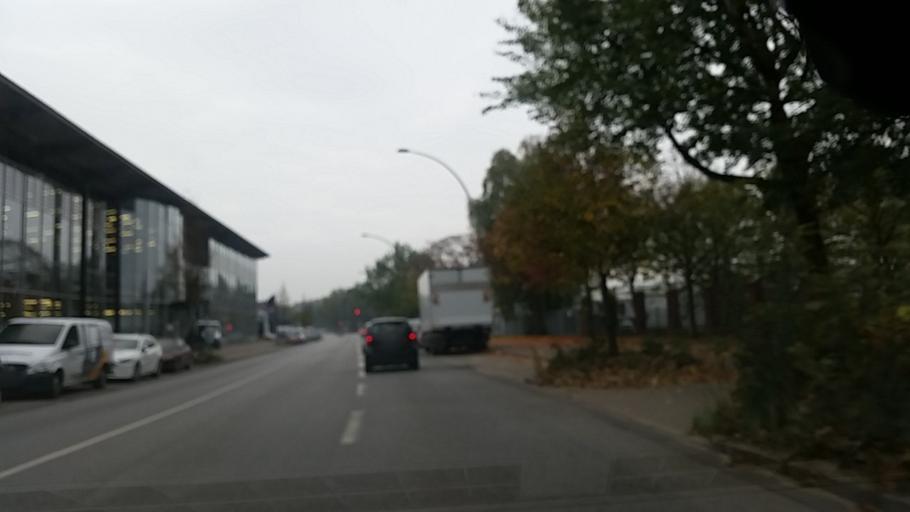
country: DE
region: Hamburg
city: Altona
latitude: 53.5696
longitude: 9.9176
